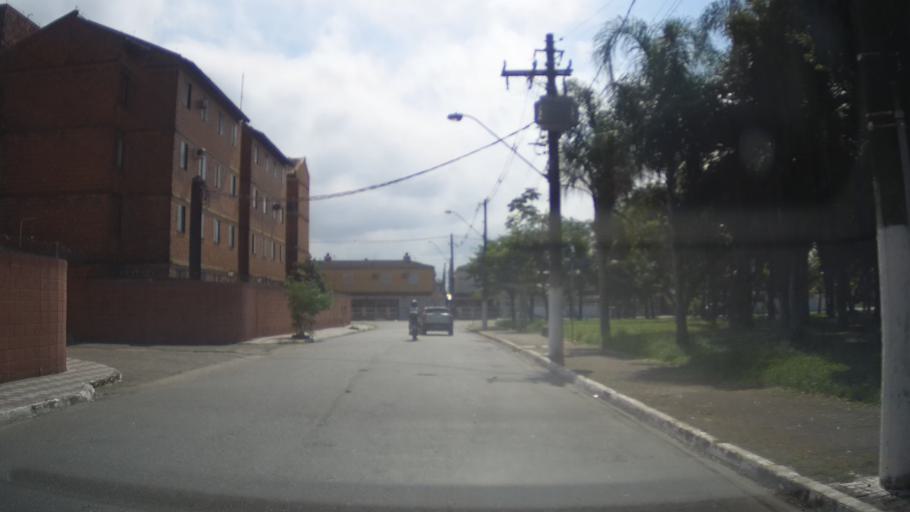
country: BR
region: Sao Paulo
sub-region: Praia Grande
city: Praia Grande
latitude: -24.0272
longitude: -46.4992
